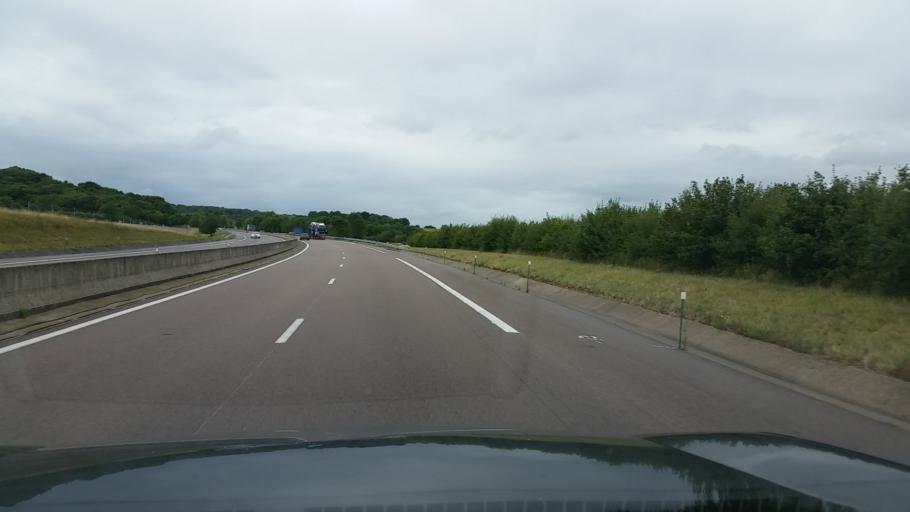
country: FR
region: Lorraine
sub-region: Departement des Vosges
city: Chatenois
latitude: 48.4045
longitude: 5.8779
